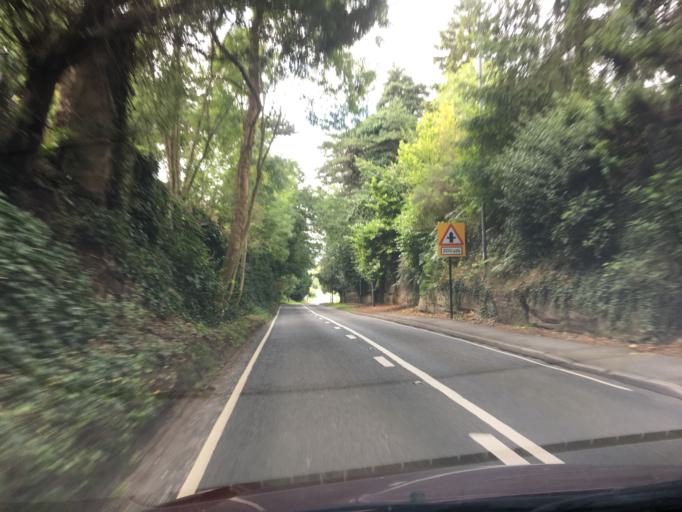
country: GB
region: England
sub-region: Warwickshire
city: Royal Leamington Spa
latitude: 52.3164
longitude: -1.5351
